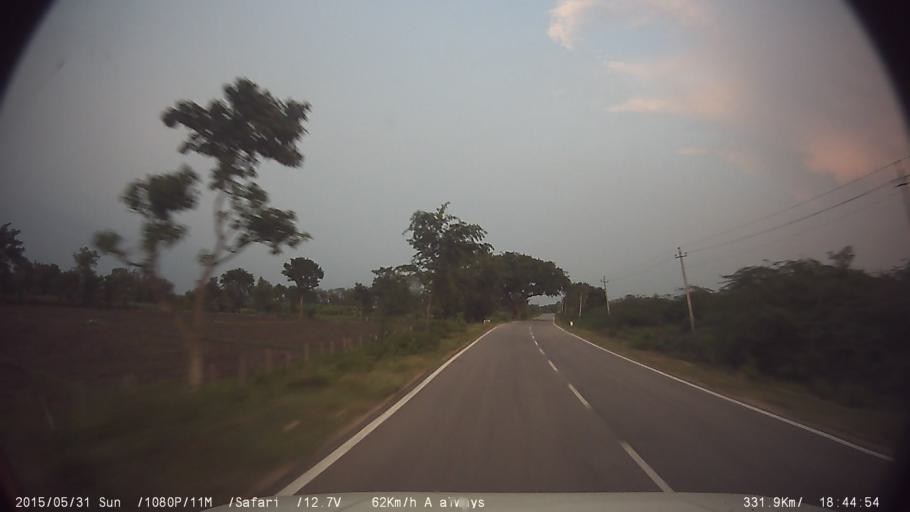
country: IN
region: Karnataka
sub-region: Mysore
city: Tirumakudal Narsipur
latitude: 12.1579
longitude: 76.8190
